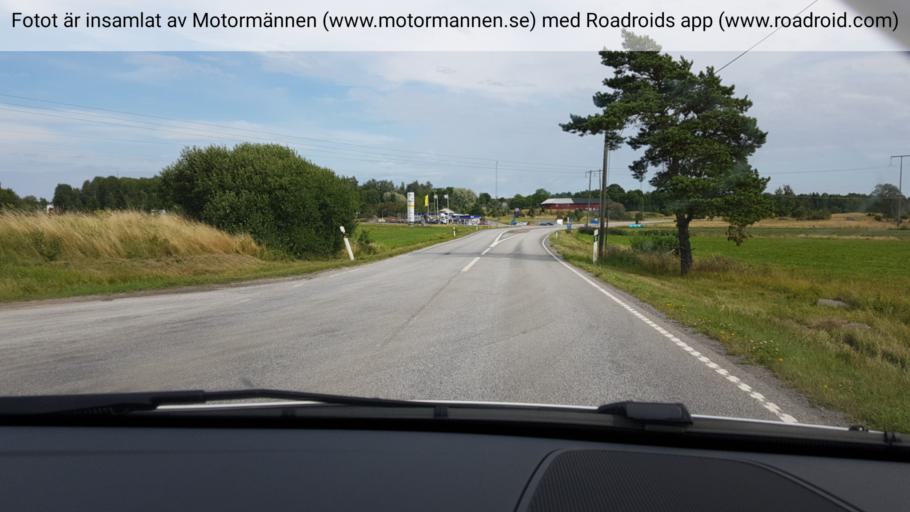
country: SE
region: Stockholm
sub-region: Norrtalje Kommun
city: Hallstavik
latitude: 60.0413
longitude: 18.5510
